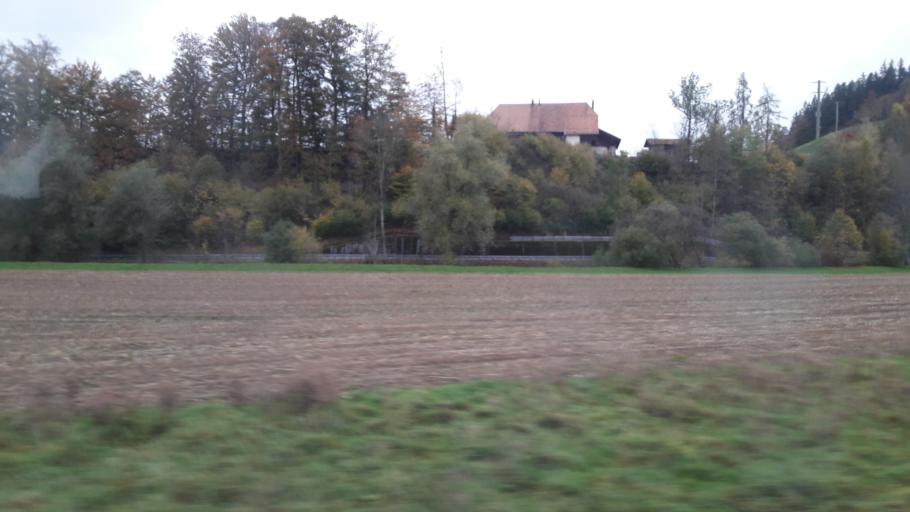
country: CH
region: Bern
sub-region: Emmental District
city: Trachselwald
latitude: 47.0133
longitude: 7.7255
